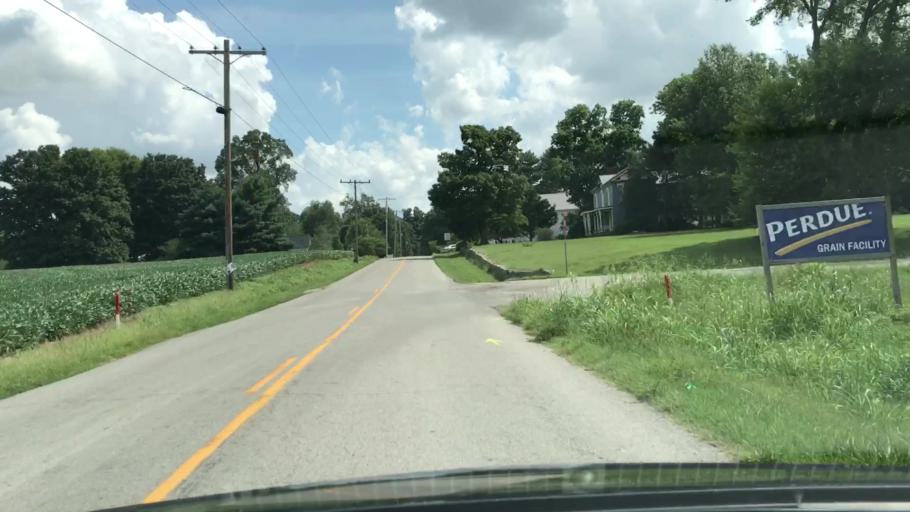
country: US
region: Kentucky
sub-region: Todd County
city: Guthrie
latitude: 36.7182
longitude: -87.0726
